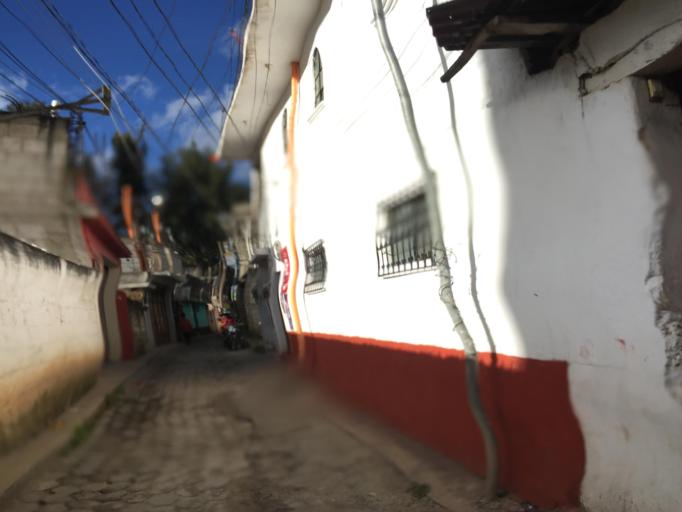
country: GT
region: Totonicapan
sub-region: Municipio de Totonicapan
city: Totonicapan
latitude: 14.9099
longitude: -91.3651
